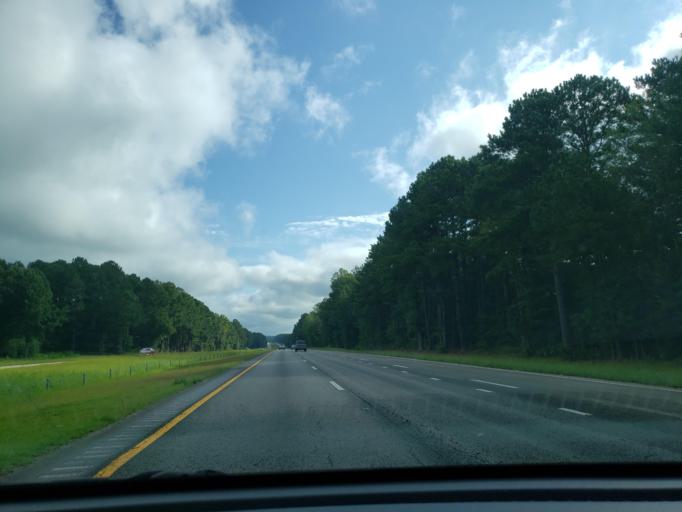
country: US
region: North Carolina
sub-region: Wake County
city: Zebulon
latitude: 35.8374
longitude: -78.3007
